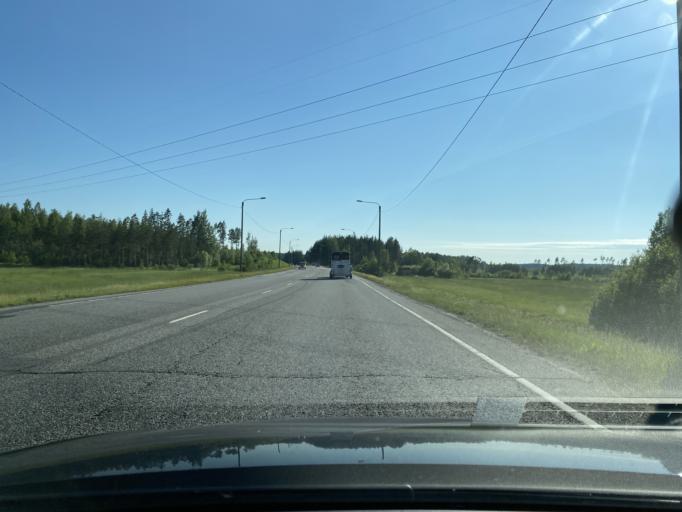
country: FI
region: Varsinais-Suomi
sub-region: Loimaa
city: Aura
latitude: 60.6140
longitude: 22.5083
